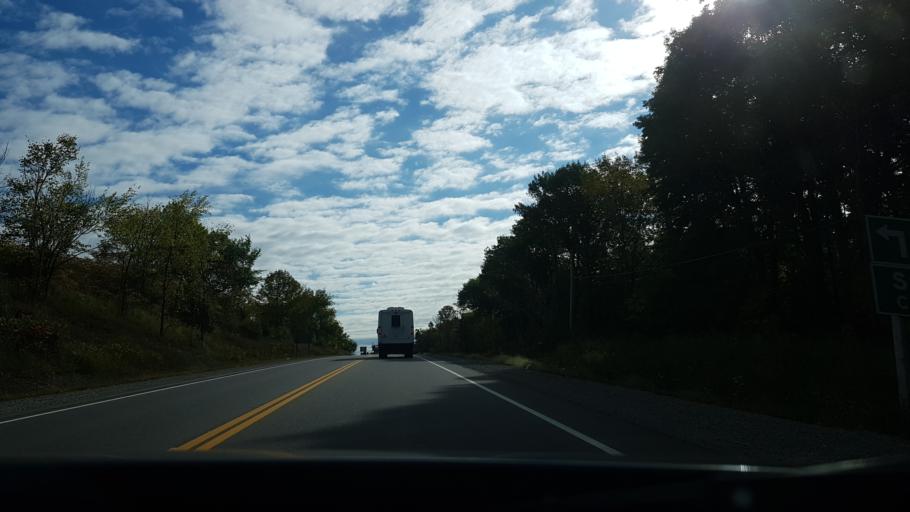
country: CA
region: Ontario
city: Orillia
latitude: 44.6135
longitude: -79.4791
